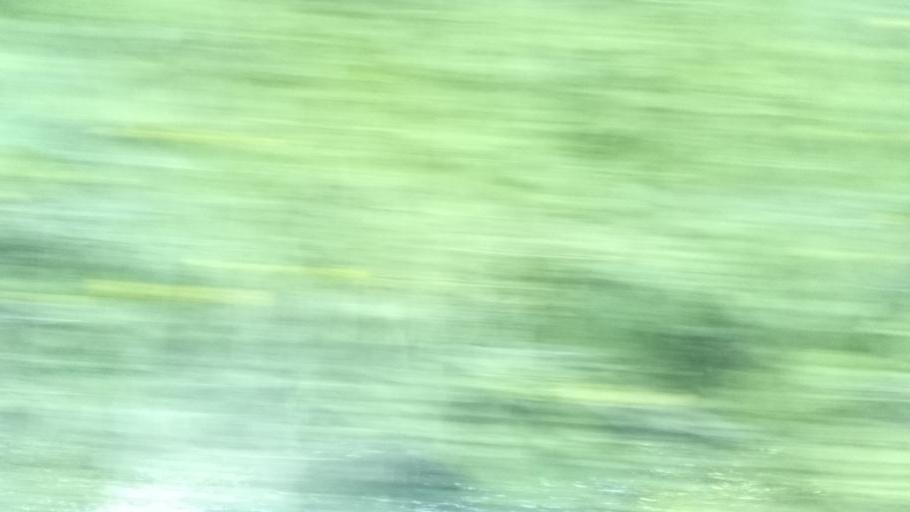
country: IT
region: Latium
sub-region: Provincia di Latina
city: Spigno Saturnia Inferiore
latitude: 41.2822
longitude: 13.7656
